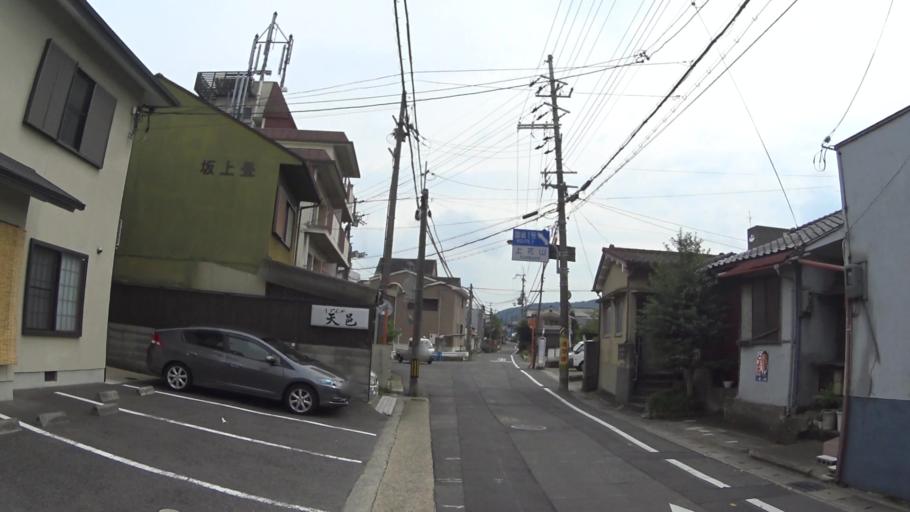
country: JP
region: Kyoto
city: Kyoto
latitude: 34.9848
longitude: 135.7989
